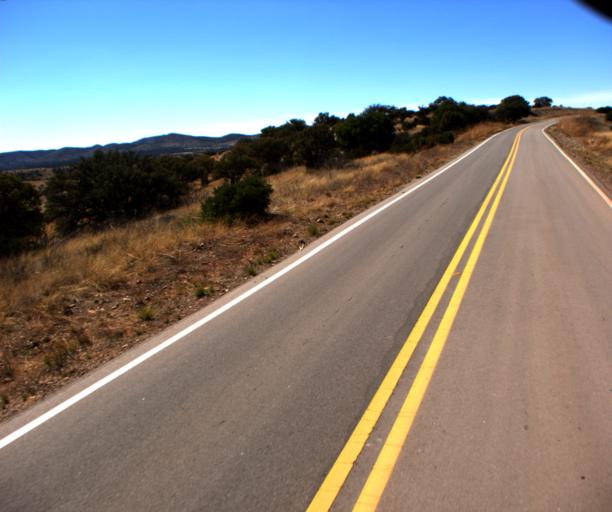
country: US
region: Arizona
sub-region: Cochise County
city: Huachuca City
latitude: 31.5234
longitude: -110.5004
